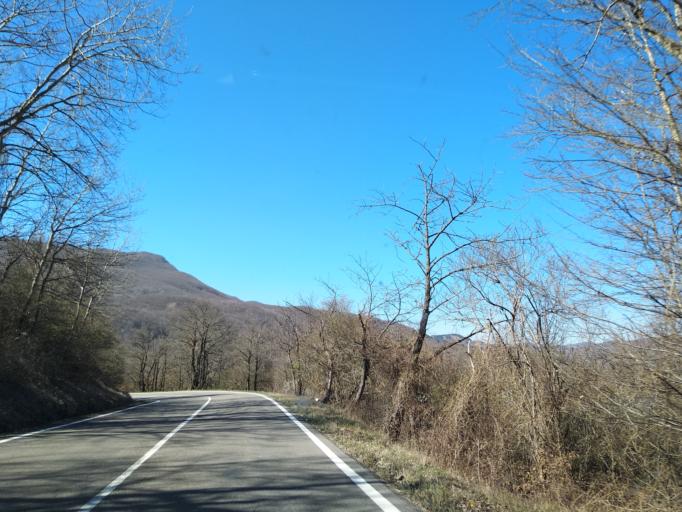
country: IT
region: Emilia-Romagna
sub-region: Provincia di Reggio Emilia
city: Busana
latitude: 44.4076
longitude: 10.3238
